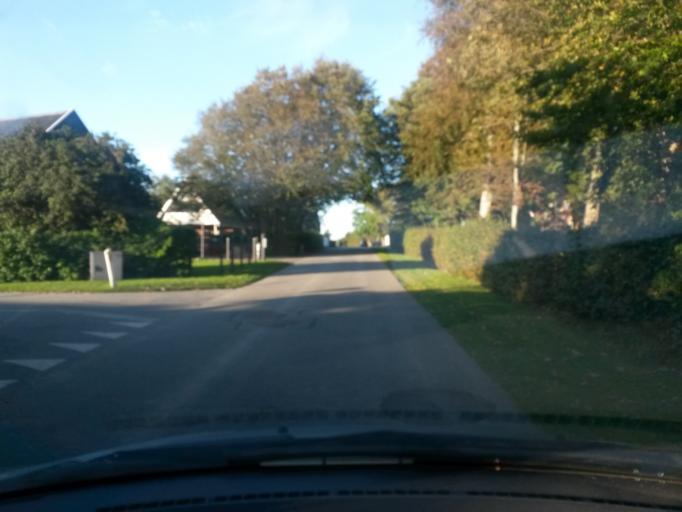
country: DK
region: Central Jutland
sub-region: Silkeborg Kommune
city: Kjellerup
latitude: 56.3281
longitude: 9.4405
